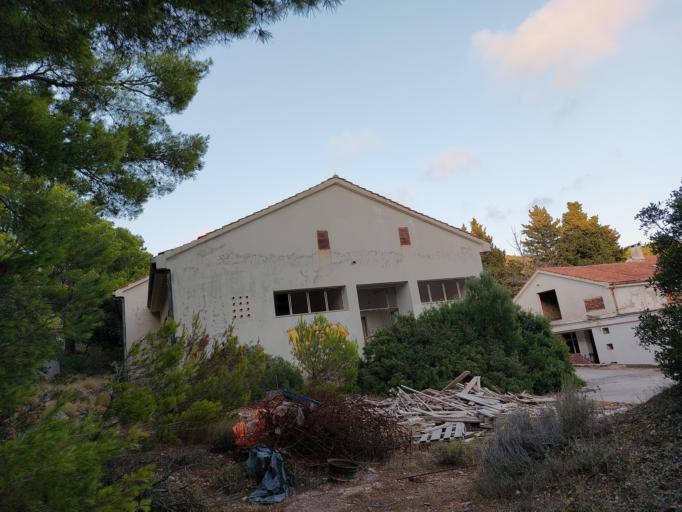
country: HR
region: Dubrovacko-Neretvanska
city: Smokvica
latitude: 42.7391
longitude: 16.8277
